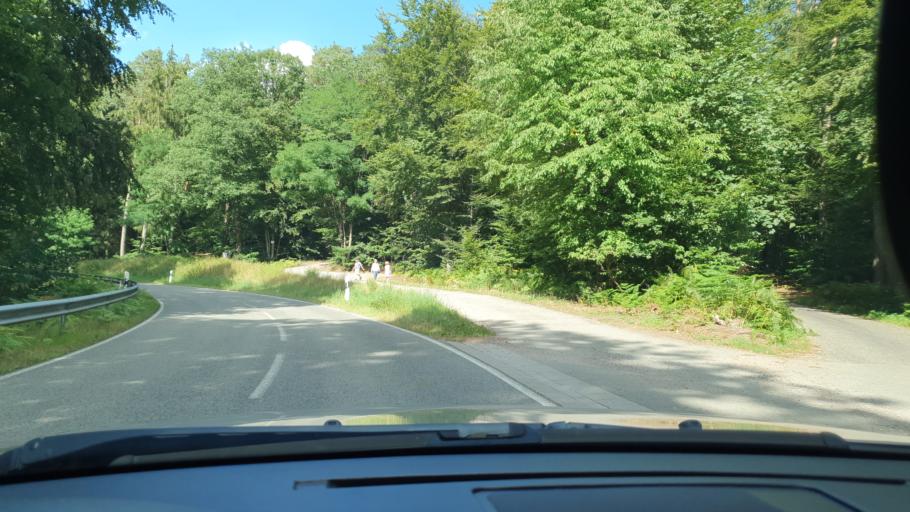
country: DE
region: Rheinland-Pfalz
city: Waldfischbach-Burgalben
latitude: 49.2888
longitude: 7.6485
